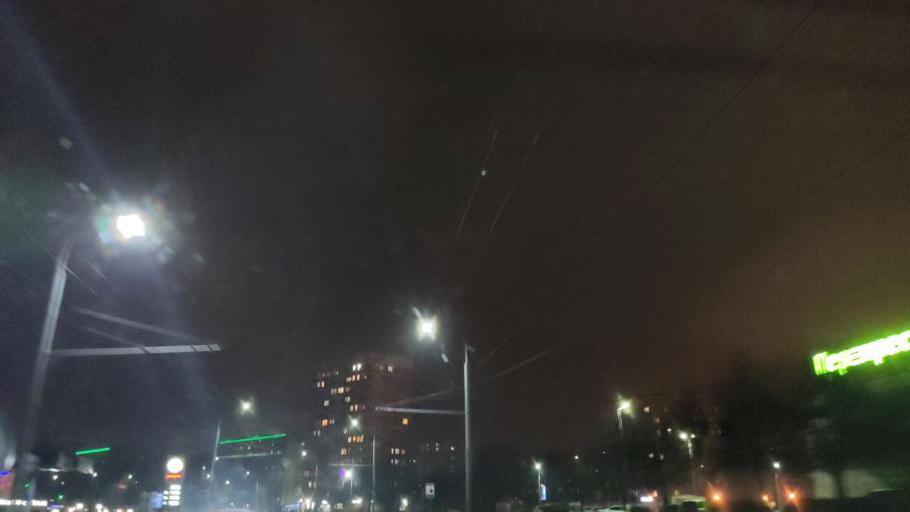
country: RU
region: Moskovskaya
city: Dubrovitsy
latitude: 55.4267
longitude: 37.5057
